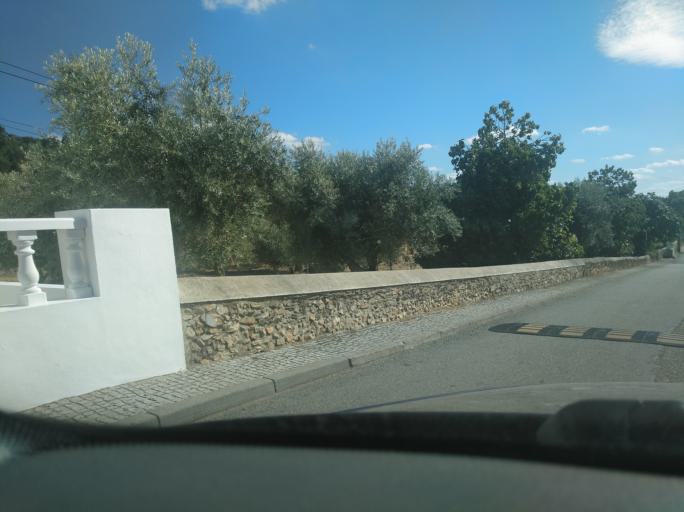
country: ES
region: Extremadura
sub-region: Provincia de Badajoz
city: La Codosera
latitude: 39.1569
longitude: -7.1930
